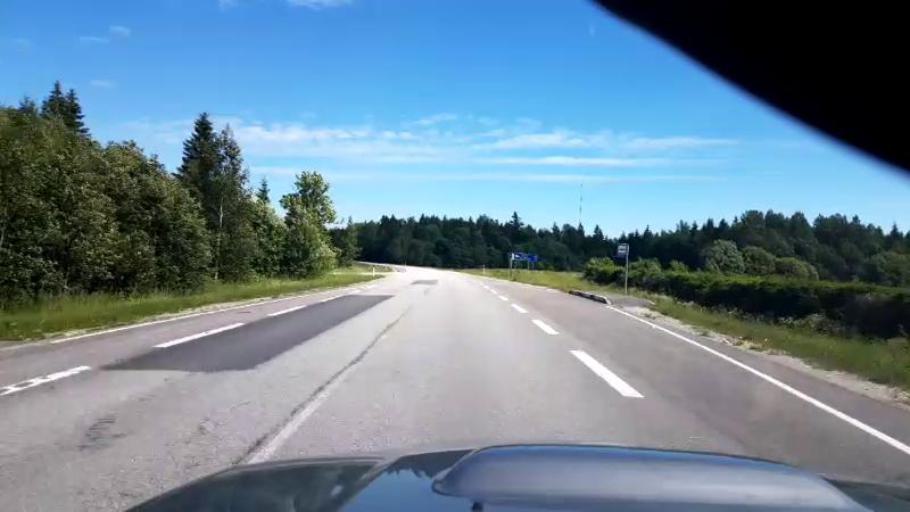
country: EE
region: Jaervamaa
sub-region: Koeru vald
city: Koeru
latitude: 58.9856
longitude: 26.0090
